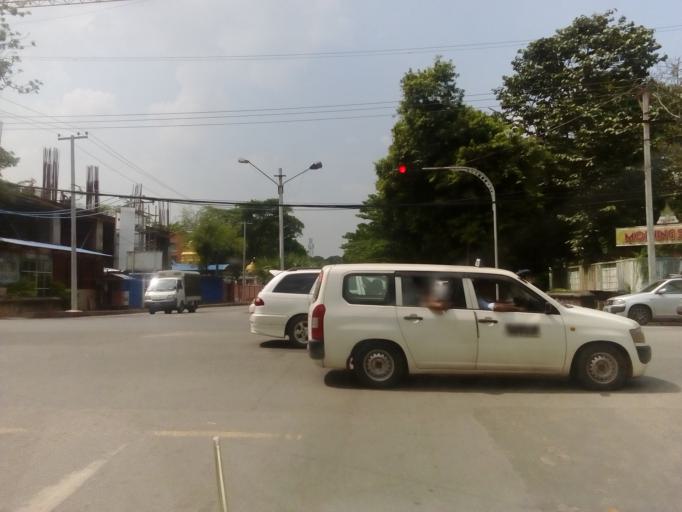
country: MM
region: Yangon
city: Yangon
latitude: 16.7892
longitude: 96.1626
